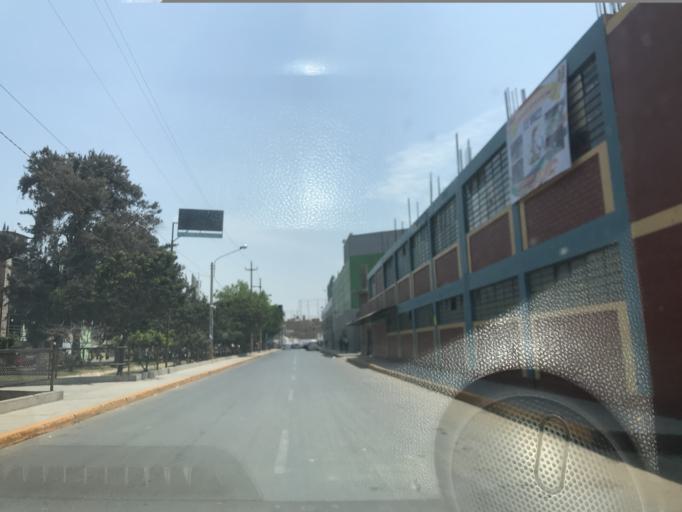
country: PE
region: Lambayeque
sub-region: Provincia de Chiclayo
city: Chiclayo
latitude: -6.7777
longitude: -79.8369
